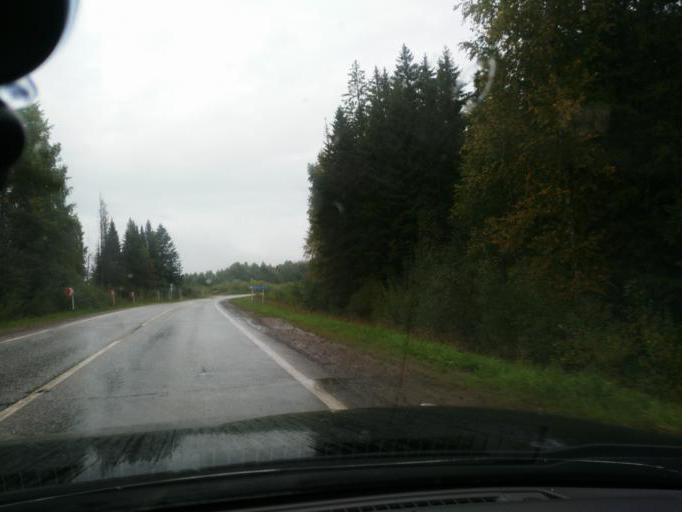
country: RU
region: Perm
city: Osa
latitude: 57.3903
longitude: 55.6089
